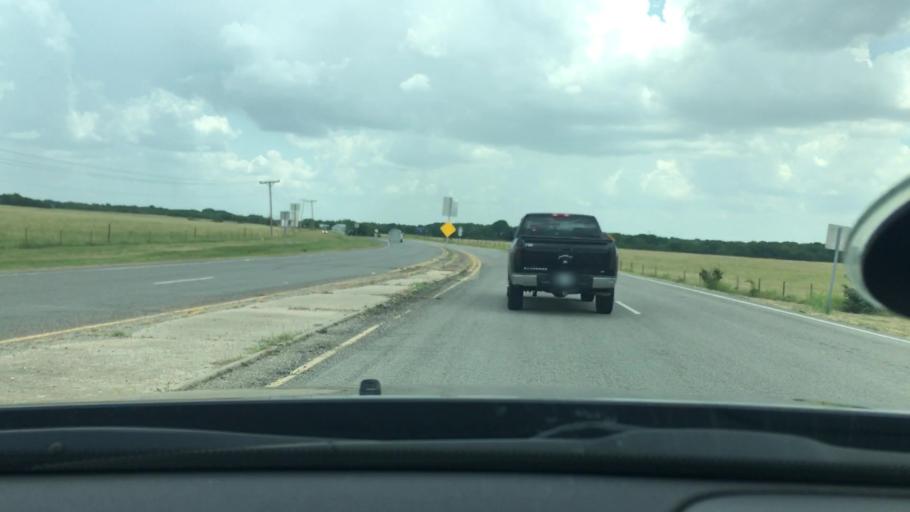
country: US
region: Oklahoma
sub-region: Marshall County
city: Madill
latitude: 34.0715
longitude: -96.7927
